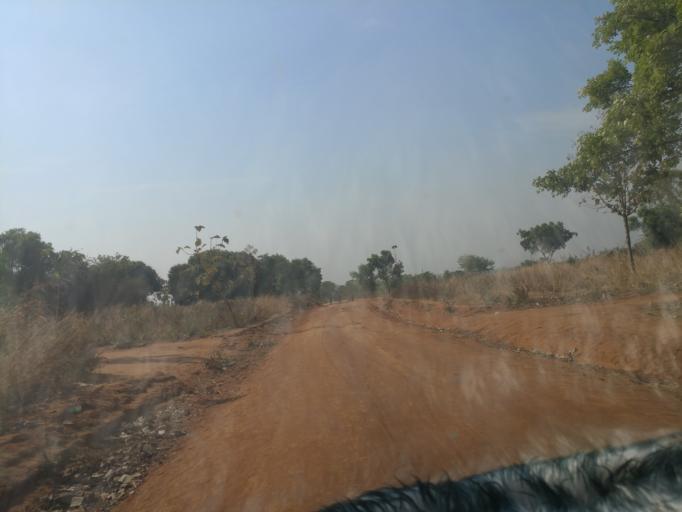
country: UG
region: Northern Region
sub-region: Yumbe District
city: Yumbe
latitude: 3.4028
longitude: 31.2360
